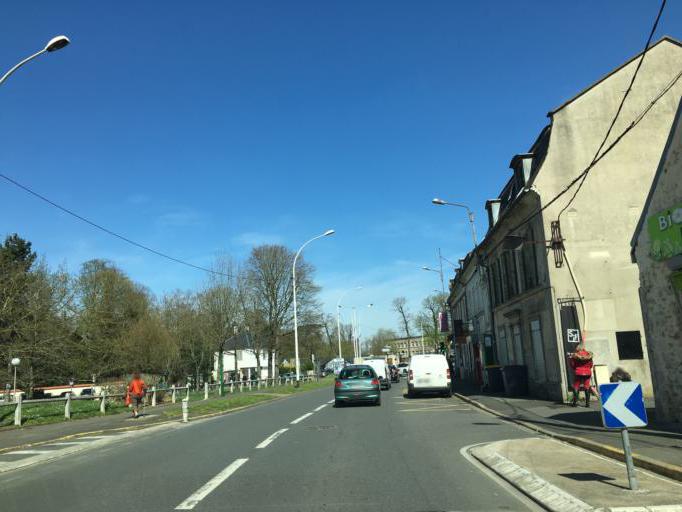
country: FR
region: Ile-de-France
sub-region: Departement de l'Essonne
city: Draveil
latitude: 48.6823
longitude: 2.4084
